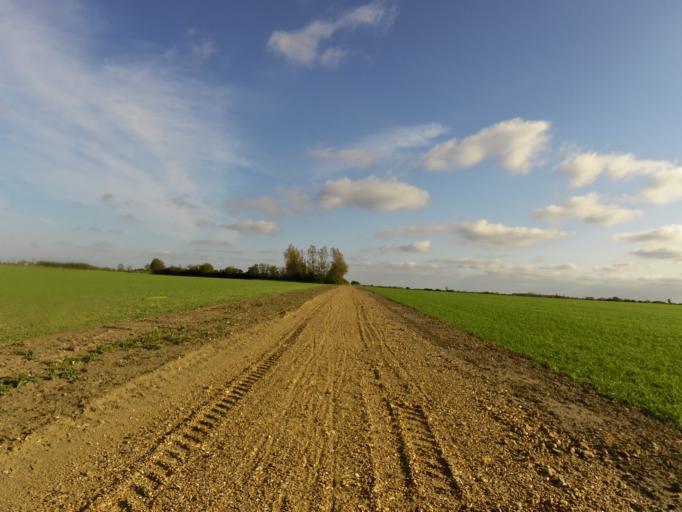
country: DK
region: South Denmark
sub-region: Vejen Kommune
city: Rodding
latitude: 55.3385
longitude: 9.0553
